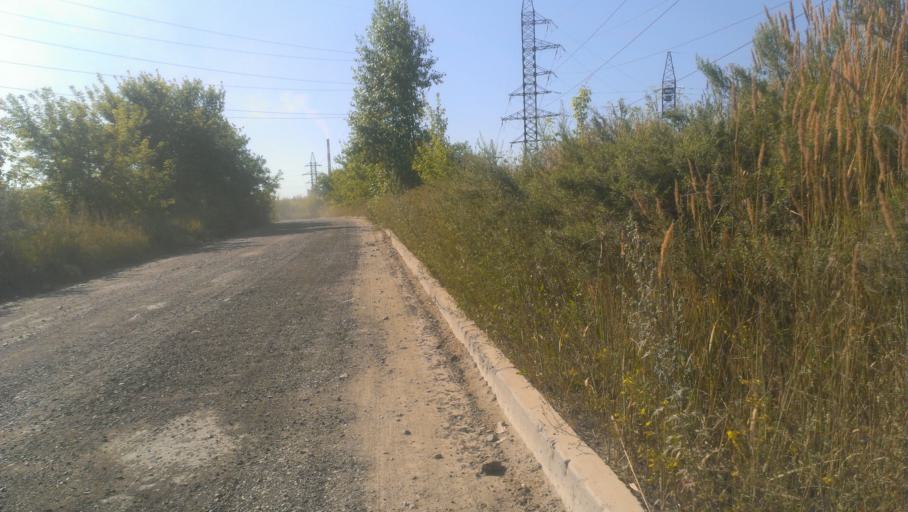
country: RU
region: Altai Krai
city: Novosilikatnyy
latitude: 53.3274
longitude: 83.6458
